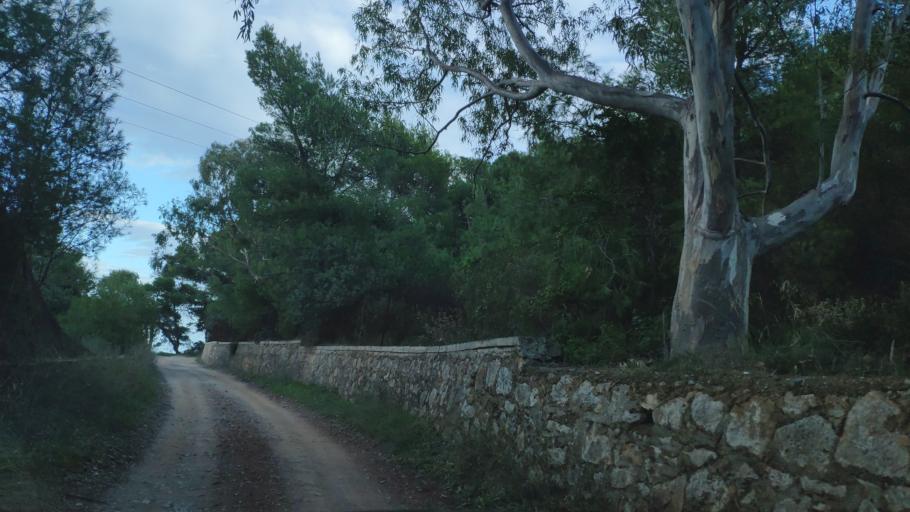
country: GR
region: Attica
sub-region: Nomarchia Anatolikis Attikis
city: Limin Mesoyaias
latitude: 37.9248
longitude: 24.0044
